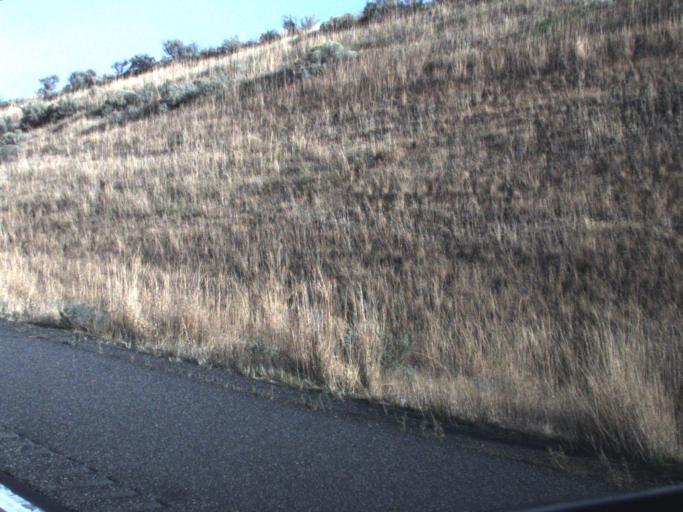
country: US
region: Oregon
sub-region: Umatilla County
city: Umatilla
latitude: 45.9981
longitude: -119.2648
